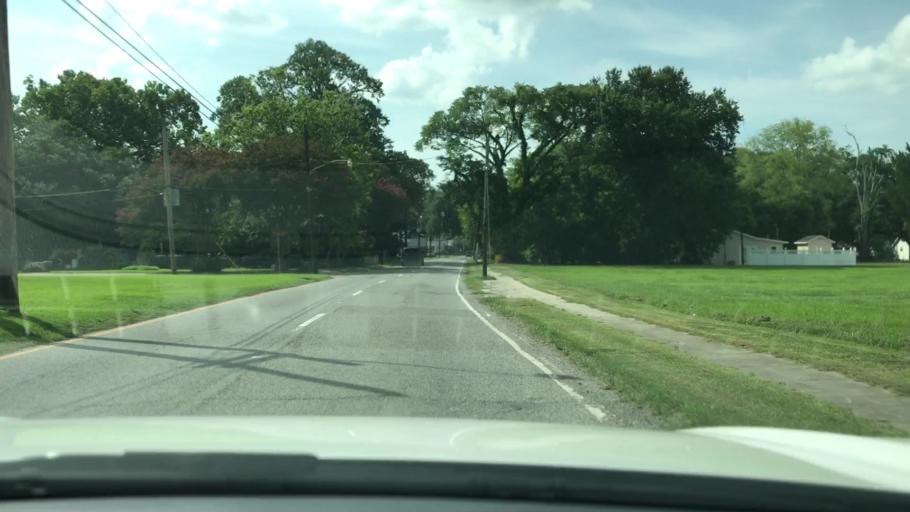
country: US
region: Louisiana
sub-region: Iberville Parish
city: Plaquemine
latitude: 30.2861
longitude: -91.2305
